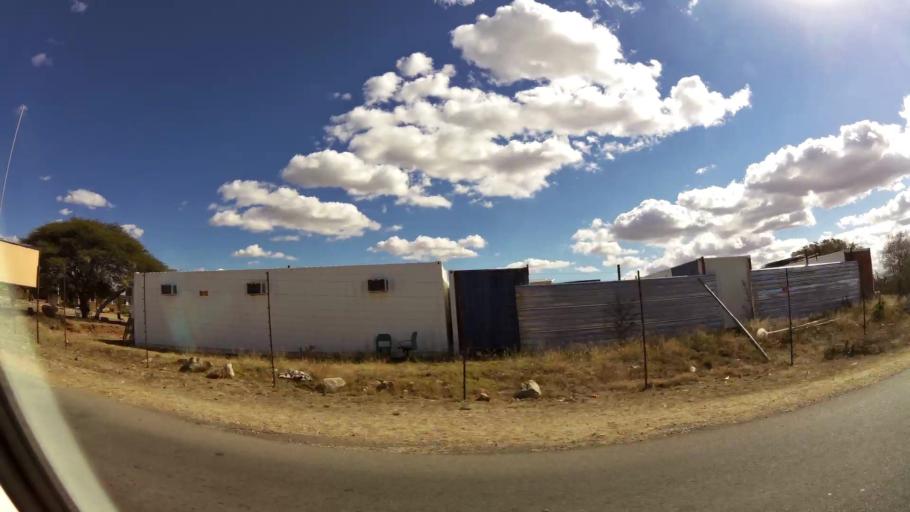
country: ZA
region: Limpopo
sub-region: Capricorn District Municipality
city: Polokwane
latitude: -23.8670
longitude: 29.5096
